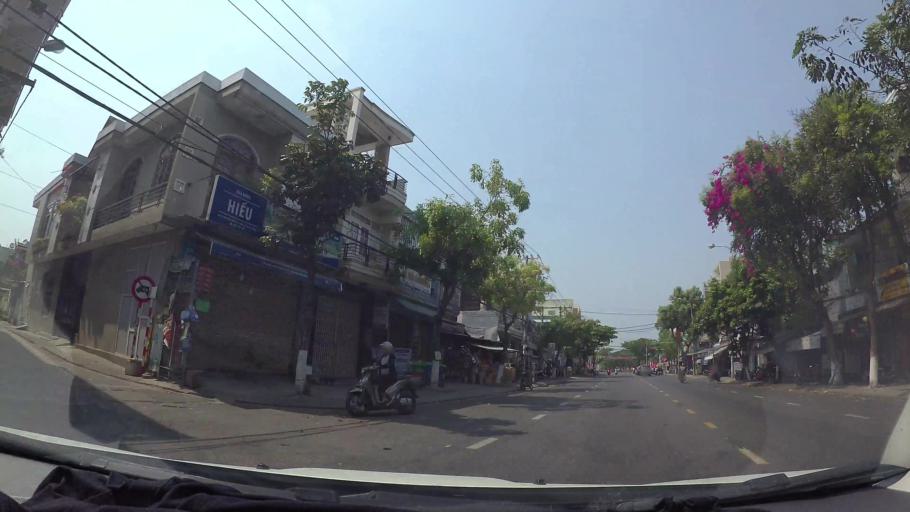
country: VN
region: Da Nang
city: Cam Le
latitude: 16.0159
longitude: 108.2050
